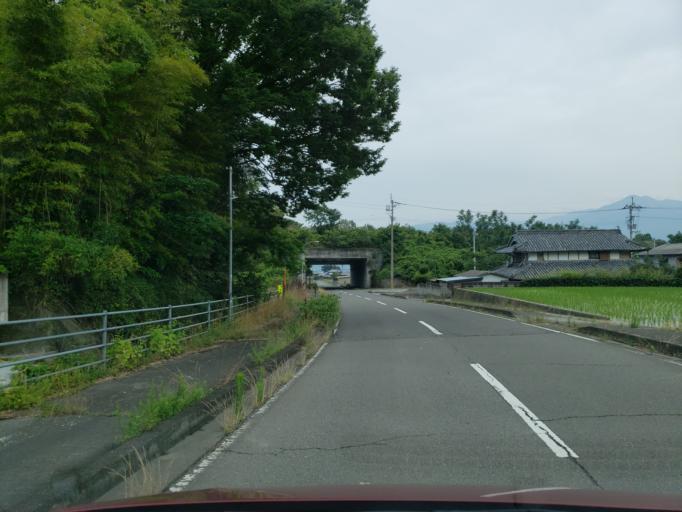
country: JP
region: Tokushima
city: Wakimachi
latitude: 34.1001
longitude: 134.2263
